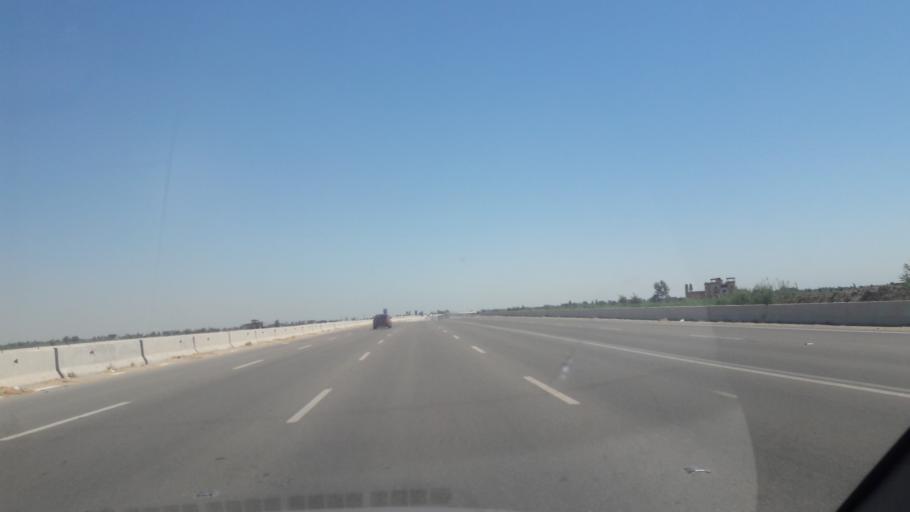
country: EG
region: Muhafazat Bur Sa`id
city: Port Said
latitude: 31.0729
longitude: 32.2344
